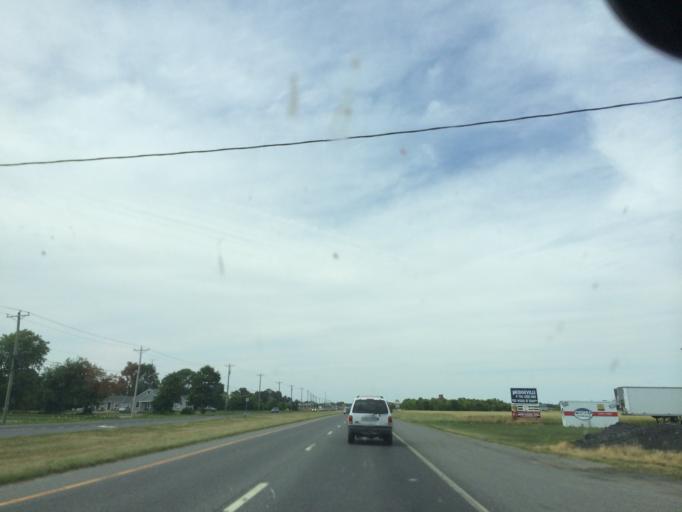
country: US
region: Delaware
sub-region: Sussex County
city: Bridgeville
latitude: 38.7153
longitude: -75.5892
